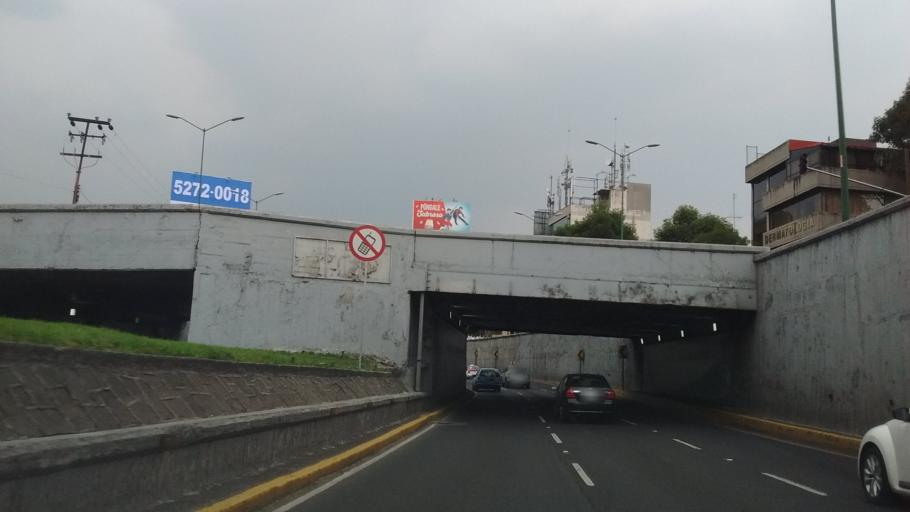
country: MX
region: Mexico City
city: Benito Juarez
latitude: 19.3992
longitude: -99.1770
